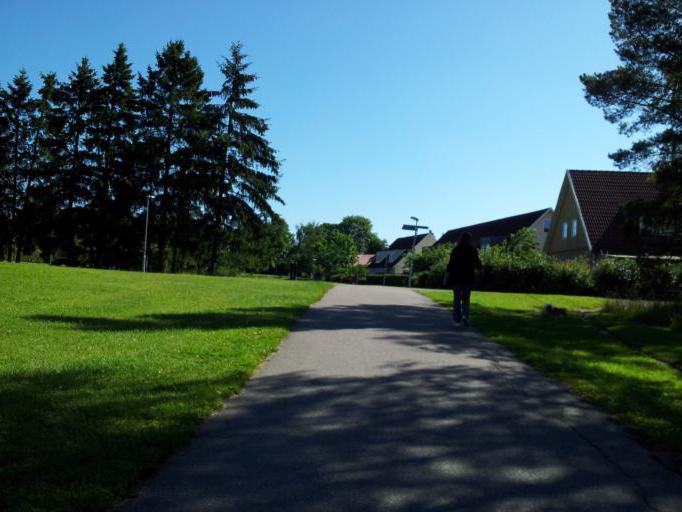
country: SE
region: Uppsala
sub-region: Uppsala Kommun
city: Saevja
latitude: 59.8674
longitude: 17.6970
